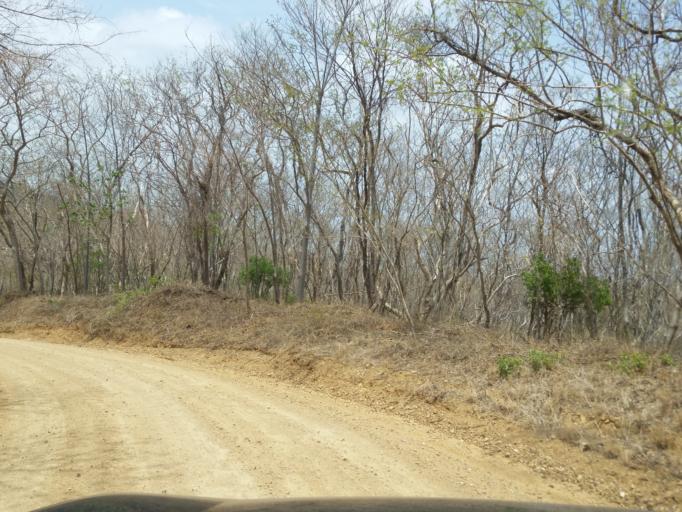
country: NI
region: Rivas
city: Tola
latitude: 11.4256
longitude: -86.0628
